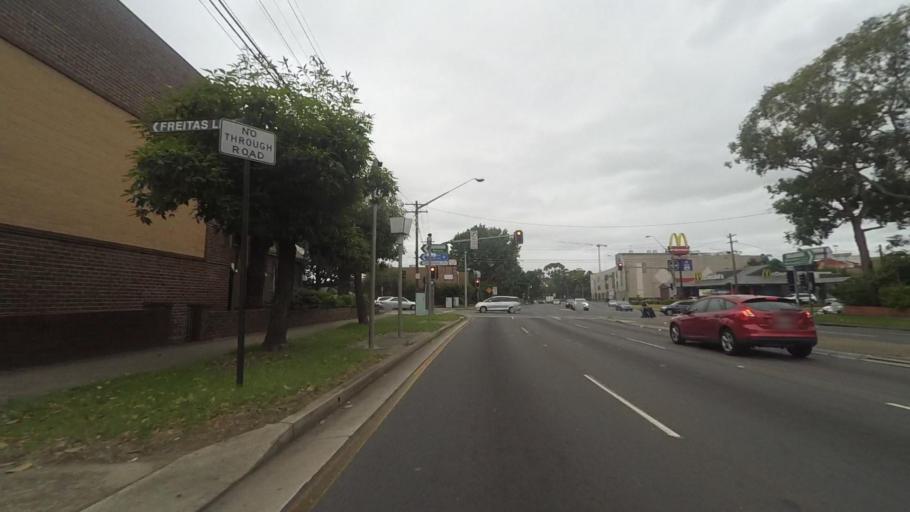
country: AU
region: New South Wales
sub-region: Auburn
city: Lidcombe
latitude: -33.8653
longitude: 151.0415
